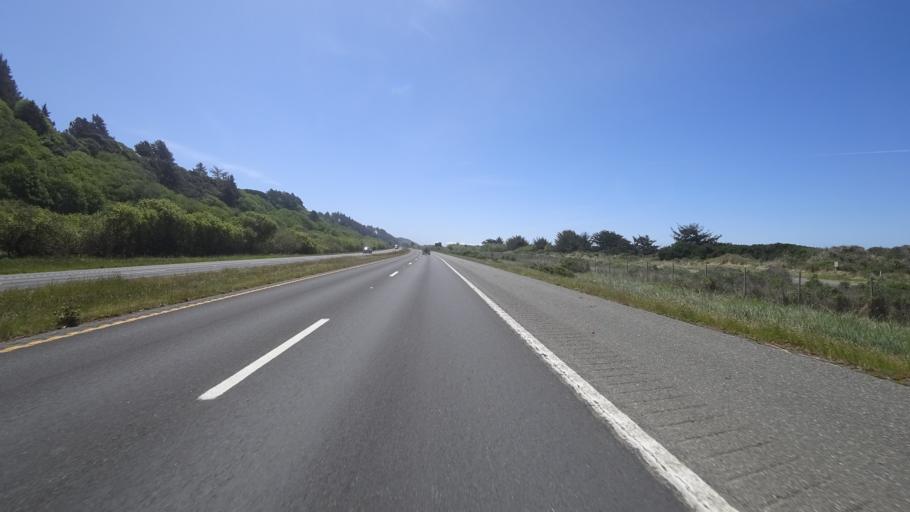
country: US
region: California
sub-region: Humboldt County
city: Westhaven-Moonstone
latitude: 41.0049
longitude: -124.1118
